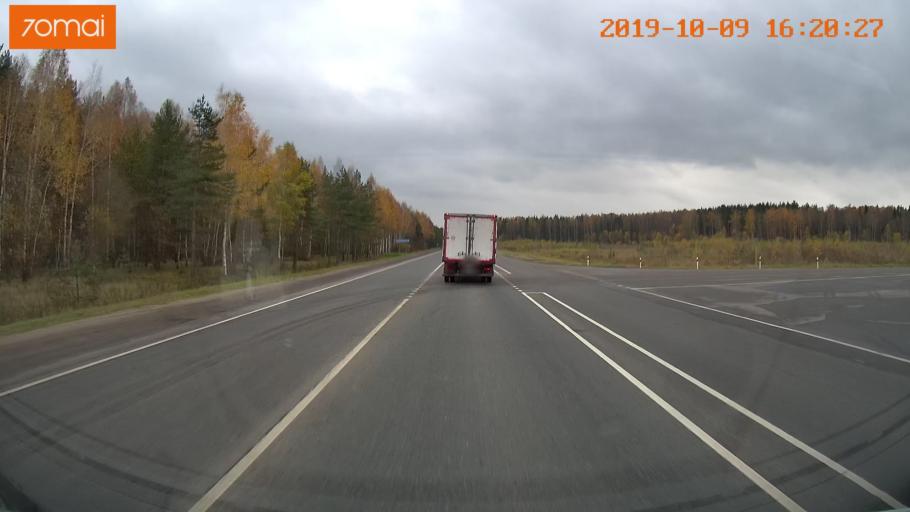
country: RU
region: Kostroma
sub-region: Kostromskoy Rayon
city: Kostroma
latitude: 57.7062
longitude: 40.8921
